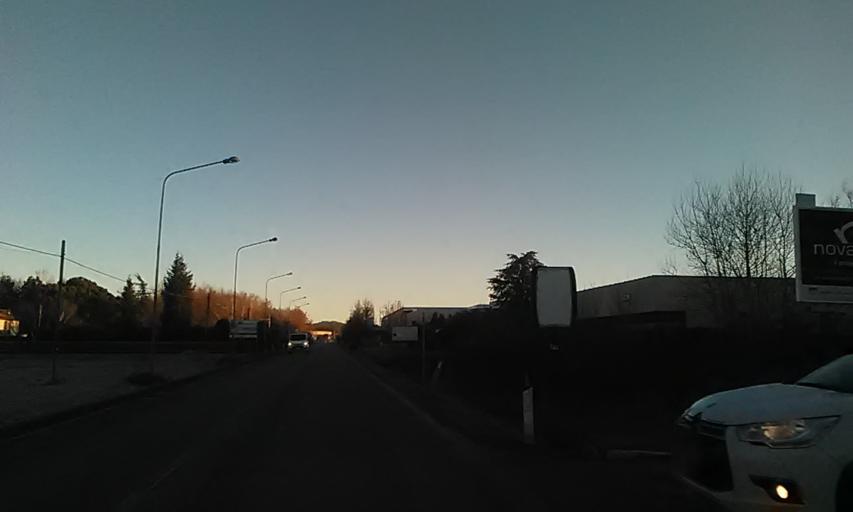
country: IT
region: Piedmont
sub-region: Provincia di Biella
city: Brusnengo
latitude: 45.5712
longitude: 8.2497
